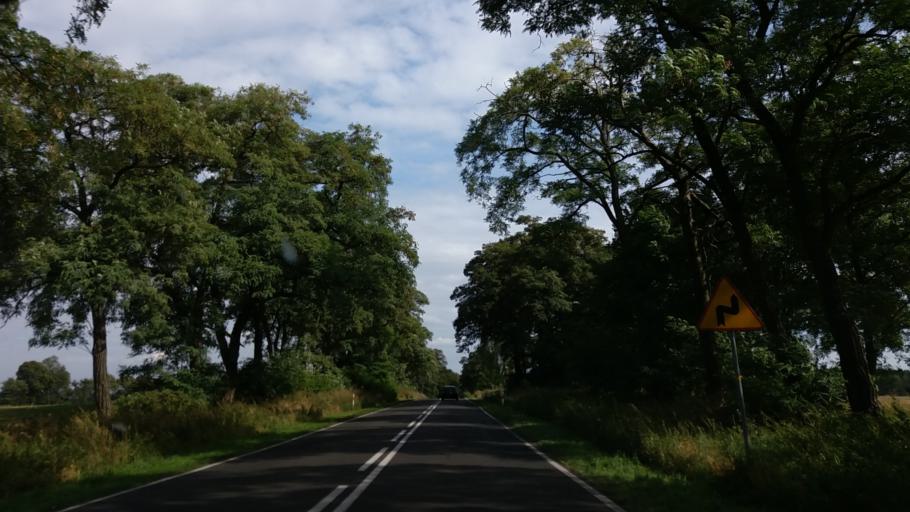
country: PL
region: West Pomeranian Voivodeship
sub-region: Powiat stargardzki
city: Suchan
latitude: 53.2022
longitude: 15.3363
